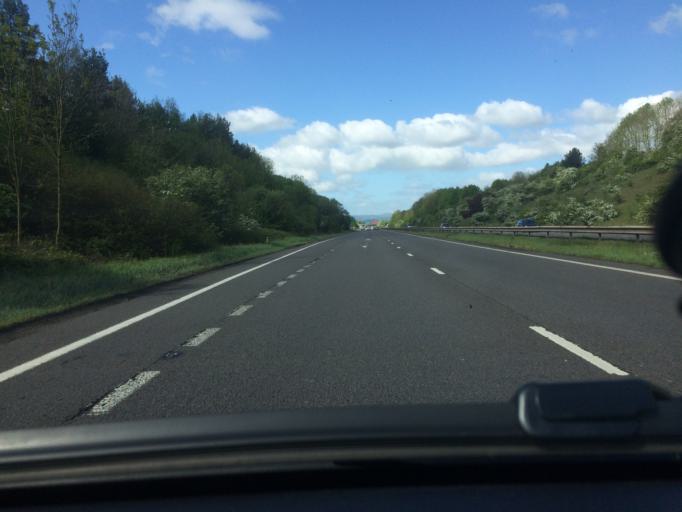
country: GB
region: England
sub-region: Cheshire West and Chester
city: Eccleston
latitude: 53.1582
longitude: -2.8937
